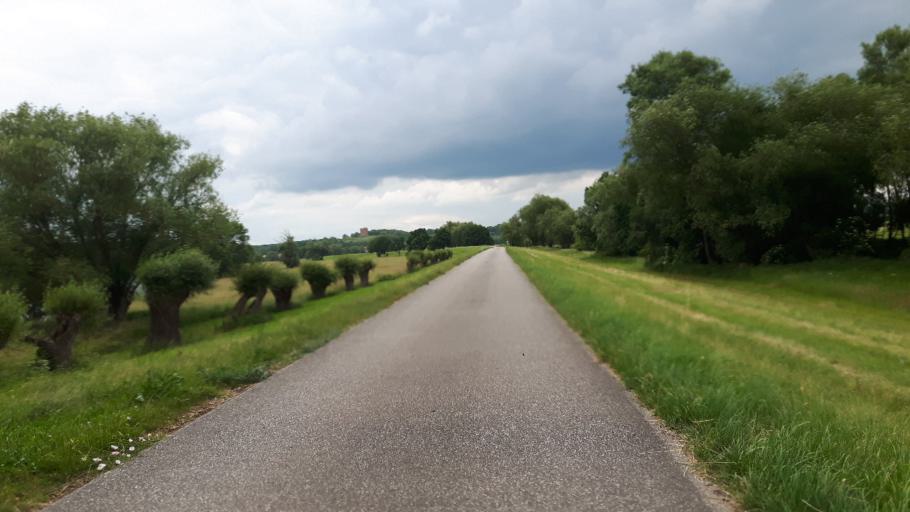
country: DE
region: Brandenburg
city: Schoneberg
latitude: 52.9654
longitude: 14.1109
